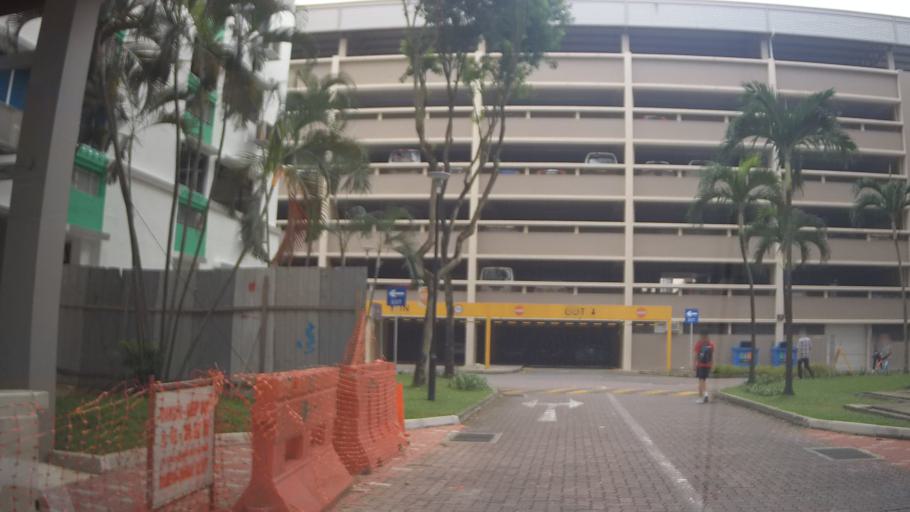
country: MY
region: Johor
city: Johor Bahru
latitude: 1.3984
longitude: 103.7463
